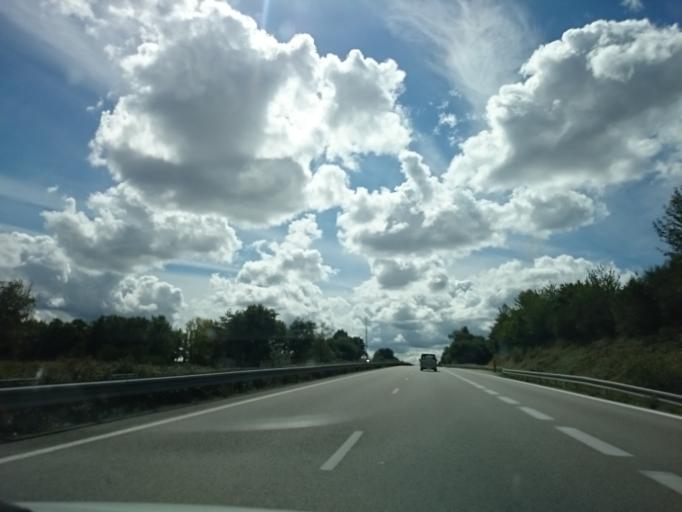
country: FR
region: Pays de la Loire
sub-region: Departement de la Loire-Atlantique
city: Mauves-sur-Loire
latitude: 47.3056
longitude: -1.4224
